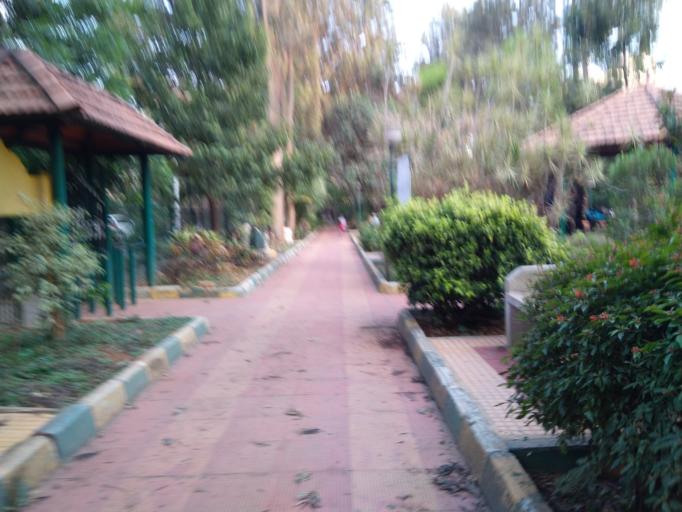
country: IN
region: Karnataka
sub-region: Bangalore Urban
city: Bangalore
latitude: 12.9105
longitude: 77.6112
